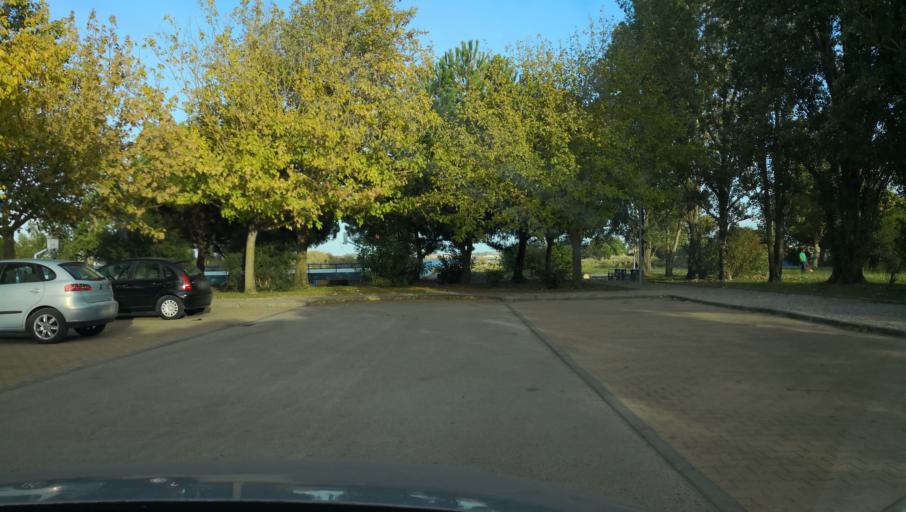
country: PT
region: Setubal
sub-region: Moita
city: Alhos Vedros
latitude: 38.6649
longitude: -9.0444
